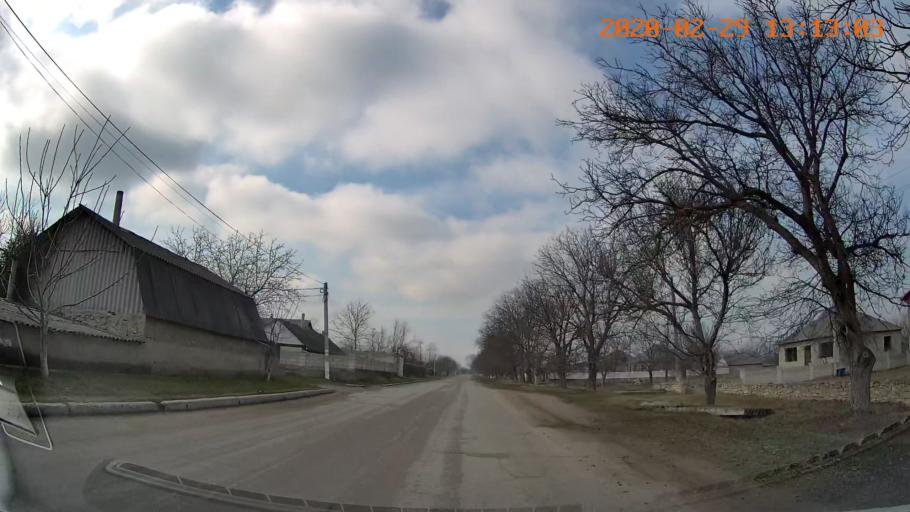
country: MD
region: Telenesti
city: Camenca
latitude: 48.0137
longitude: 28.6888
